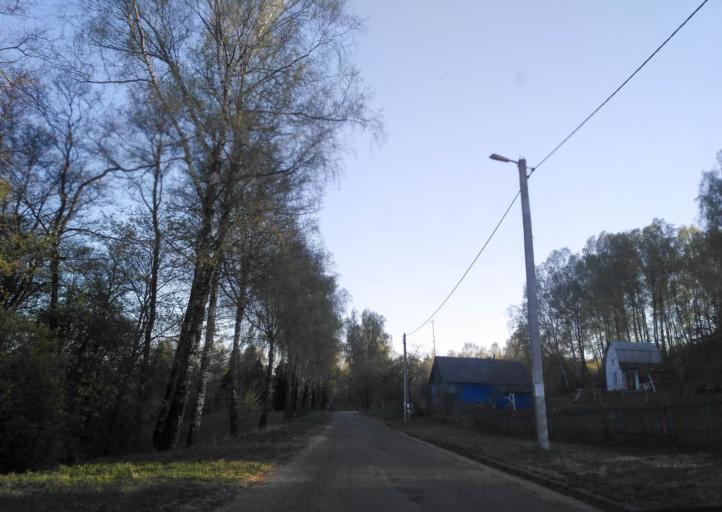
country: BY
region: Minsk
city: Pyatryshki
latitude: 54.0938
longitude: 27.1942
